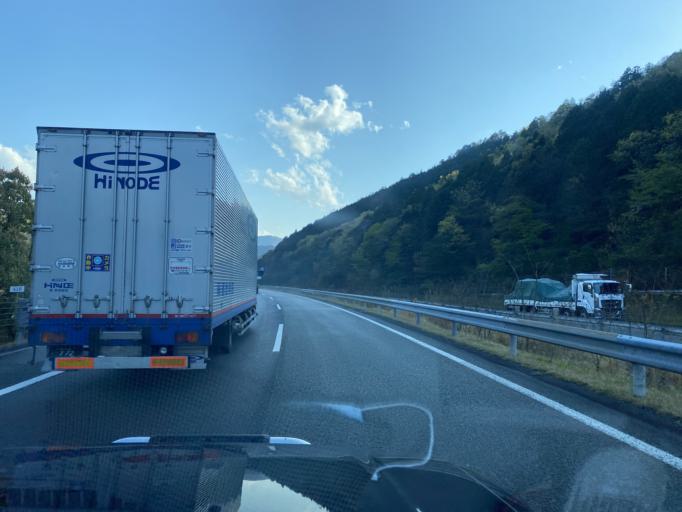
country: JP
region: Kyoto
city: Fukuchiyama
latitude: 35.2102
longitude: 135.1655
